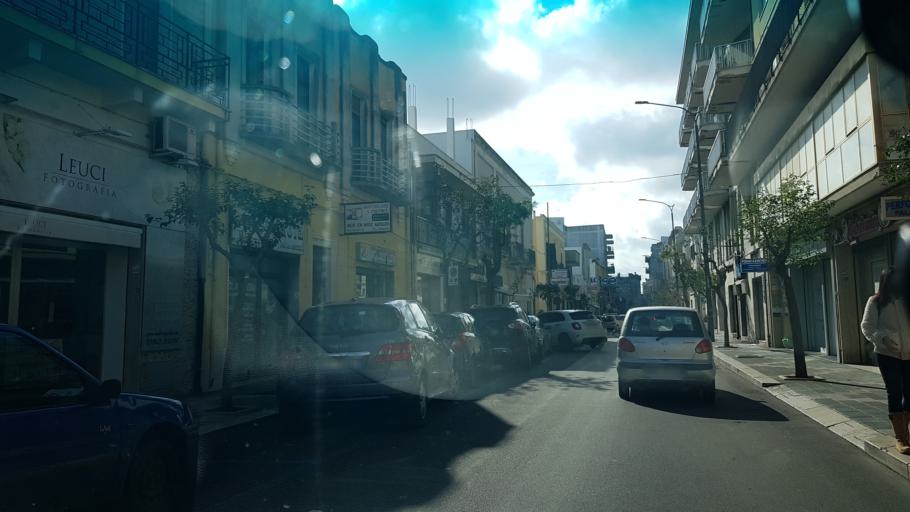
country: IT
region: Apulia
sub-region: Provincia di Brindisi
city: San Pietro Vernotico
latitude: 40.4905
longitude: 17.9965
